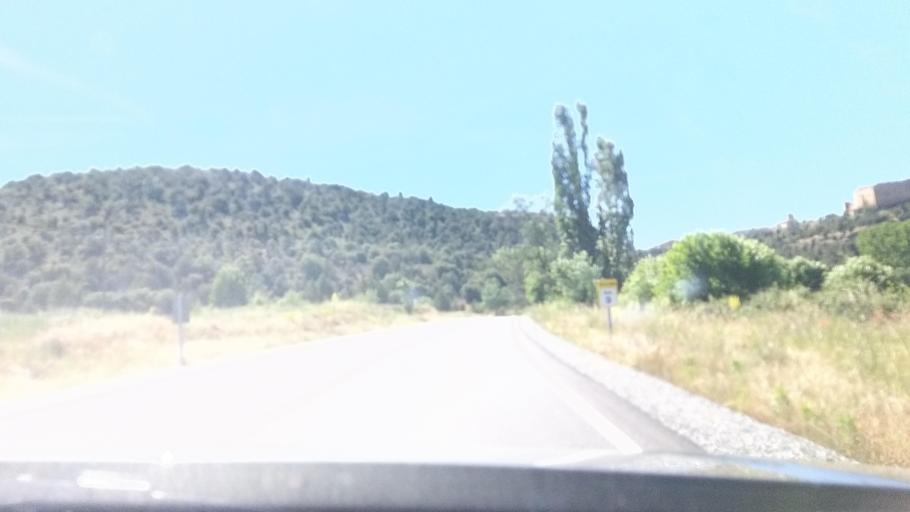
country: ES
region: Castille and Leon
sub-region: Provincia de Segovia
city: Pedraza
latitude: 41.1385
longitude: -3.8172
